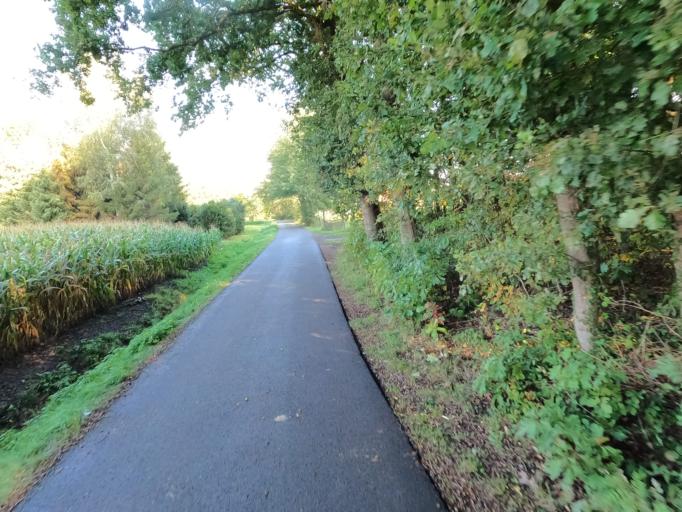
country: BE
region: Flanders
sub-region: Provincie Antwerpen
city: Zandhoven
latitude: 51.2229
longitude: 4.6593
